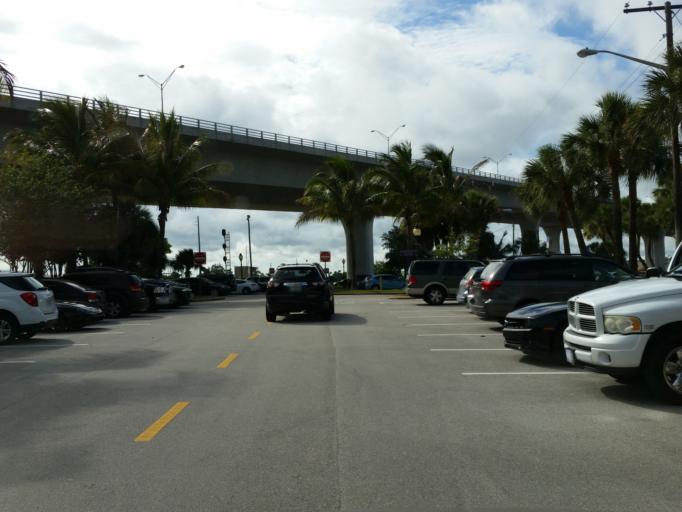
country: US
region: Florida
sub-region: Martin County
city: Stuart
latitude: 27.2014
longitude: -80.2570
